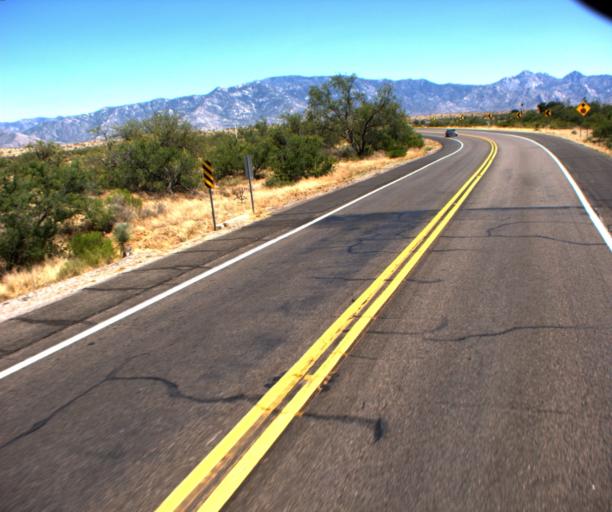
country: US
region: Arizona
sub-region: Pima County
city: Catalina
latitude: 32.5586
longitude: -110.9355
